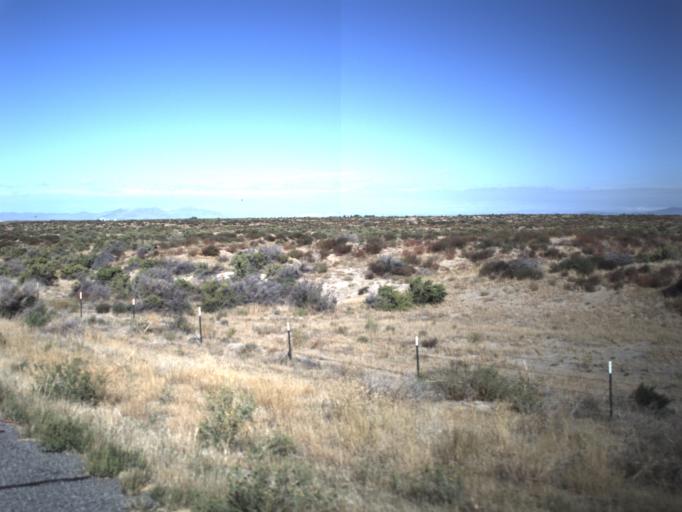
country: US
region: Utah
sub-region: Millard County
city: Delta
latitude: 39.3534
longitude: -112.4791
